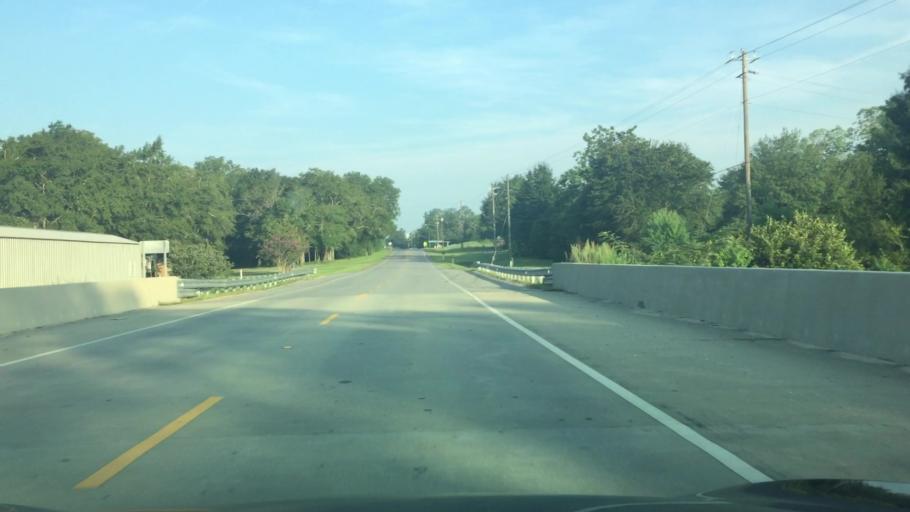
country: US
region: Alabama
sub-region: Covington County
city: Florala
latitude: 31.0095
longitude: -86.3458
